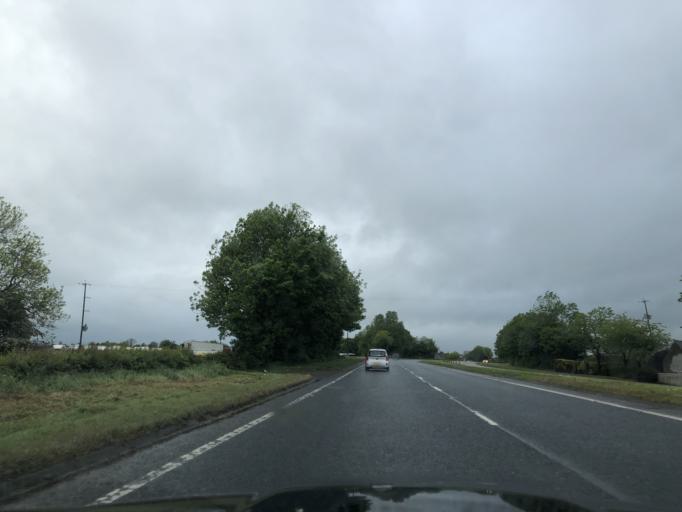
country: GB
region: Northern Ireland
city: Randalstown
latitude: 54.7642
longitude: -6.2447
